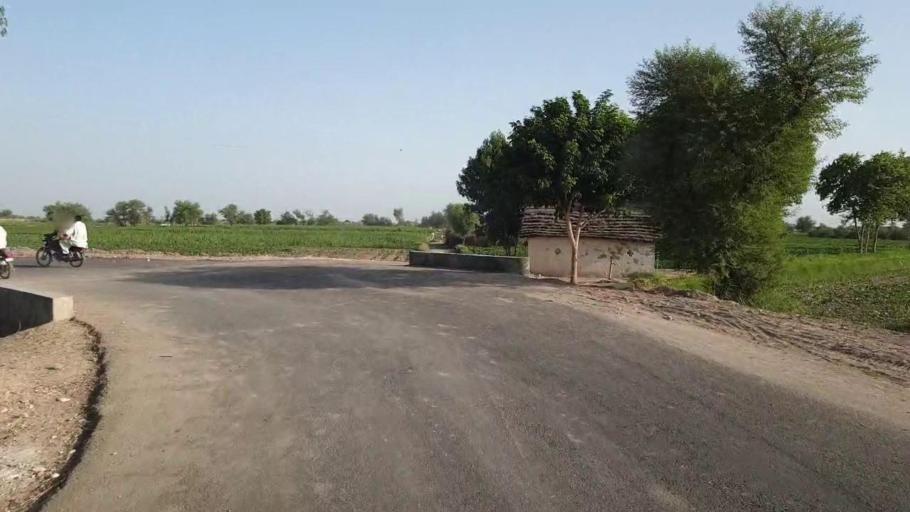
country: PK
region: Sindh
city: Jam Sahib
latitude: 26.3419
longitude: 68.5688
